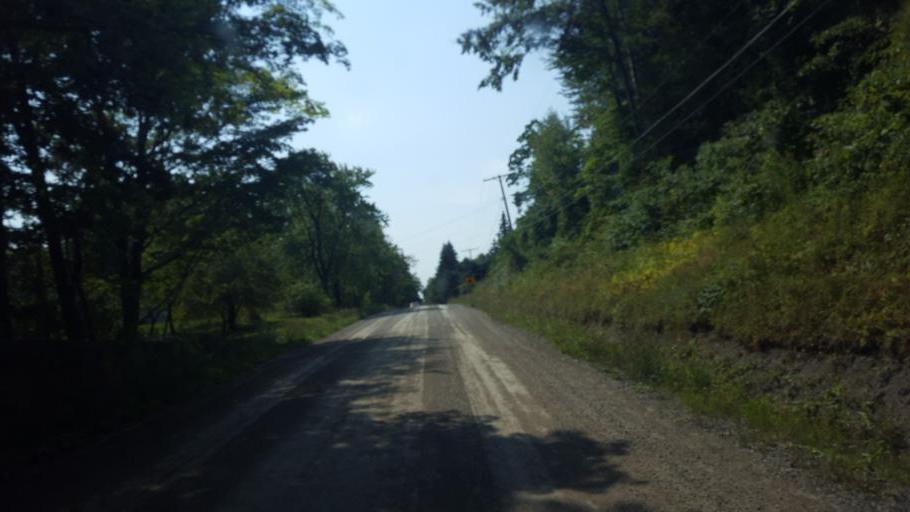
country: US
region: Ohio
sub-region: Lake County
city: Madison
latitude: 41.6922
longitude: -81.0382
